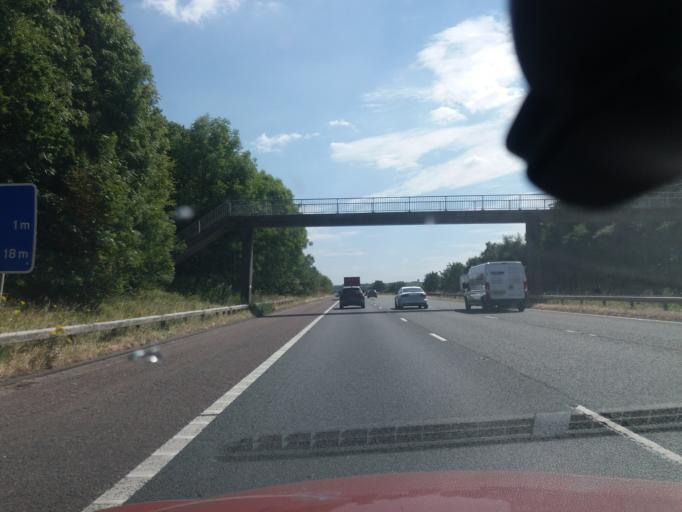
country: GB
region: England
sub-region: Borough of Wigan
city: Haigh
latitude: 53.6174
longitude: -2.5842
